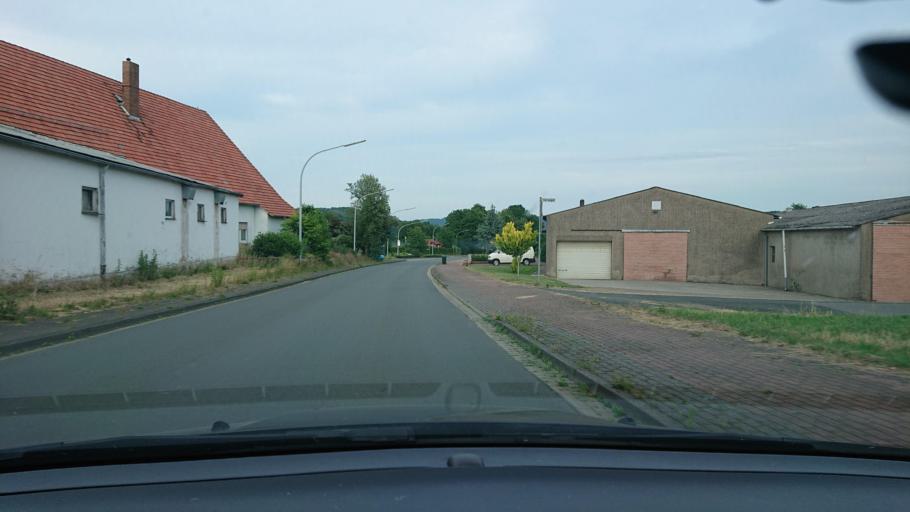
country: DE
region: North Rhine-Westphalia
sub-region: Regierungsbezirk Detmold
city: Rodinghausen
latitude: 52.2798
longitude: 8.4749
